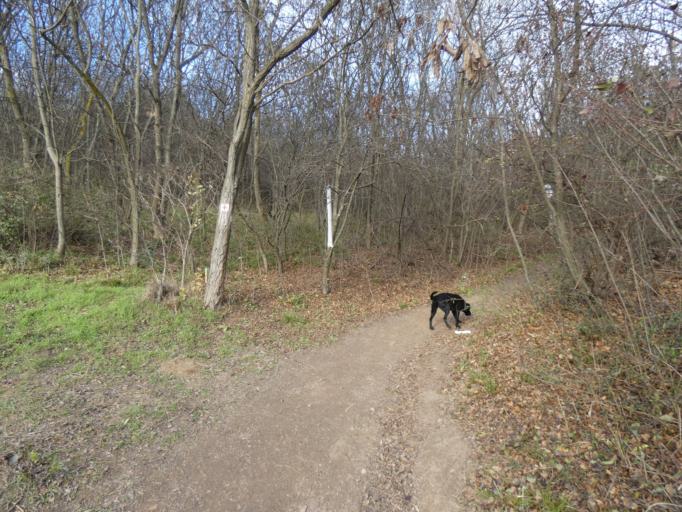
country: HU
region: Pest
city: Budaors
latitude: 47.4702
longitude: 18.9341
